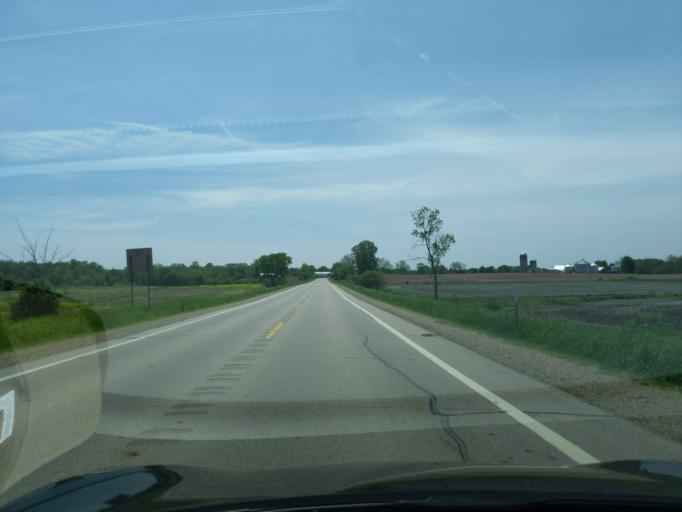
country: US
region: Michigan
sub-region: Ingham County
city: Stockbridge
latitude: 42.3993
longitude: -84.2427
